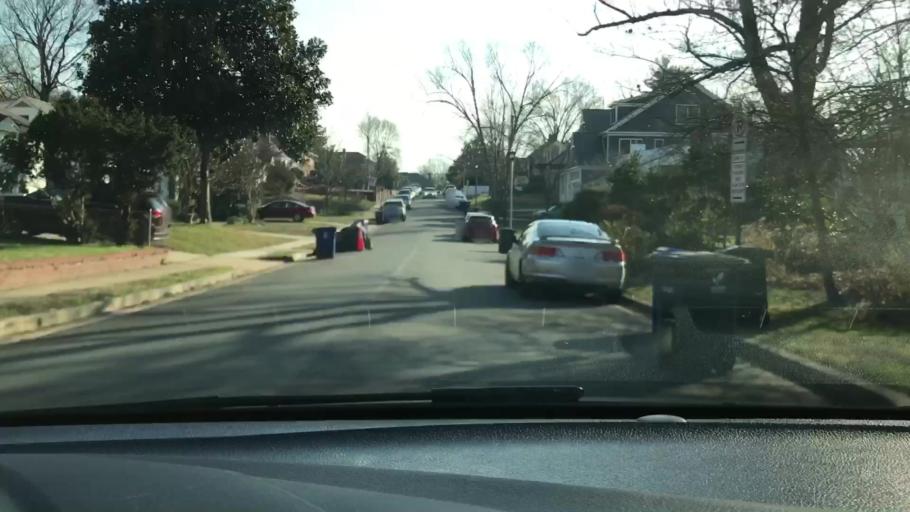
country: US
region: Virginia
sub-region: Arlington County
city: Arlington
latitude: 38.8776
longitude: -77.1154
